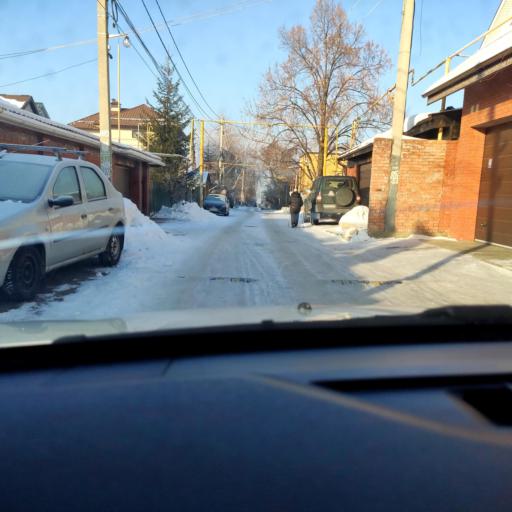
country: RU
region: Samara
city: Samara
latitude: 53.2720
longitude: 50.2032
